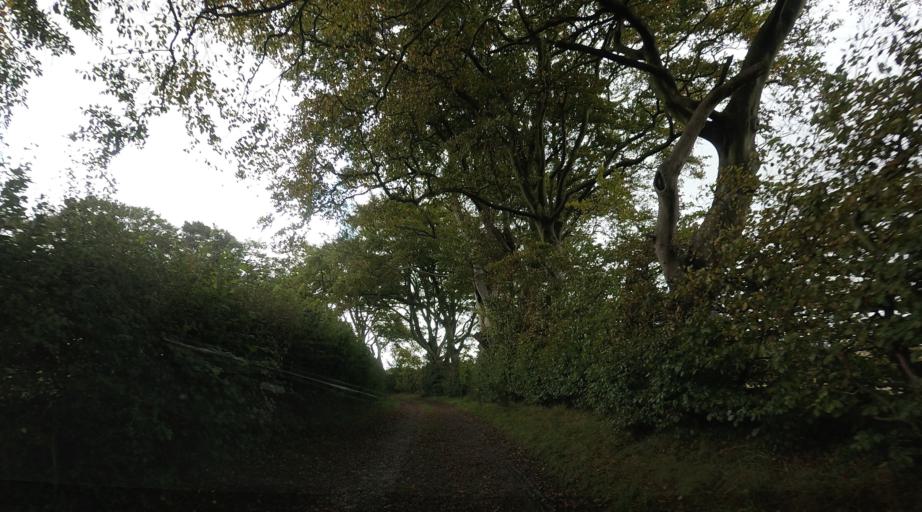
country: GB
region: Scotland
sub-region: Fife
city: Balmullo
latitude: 56.3727
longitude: -2.9559
